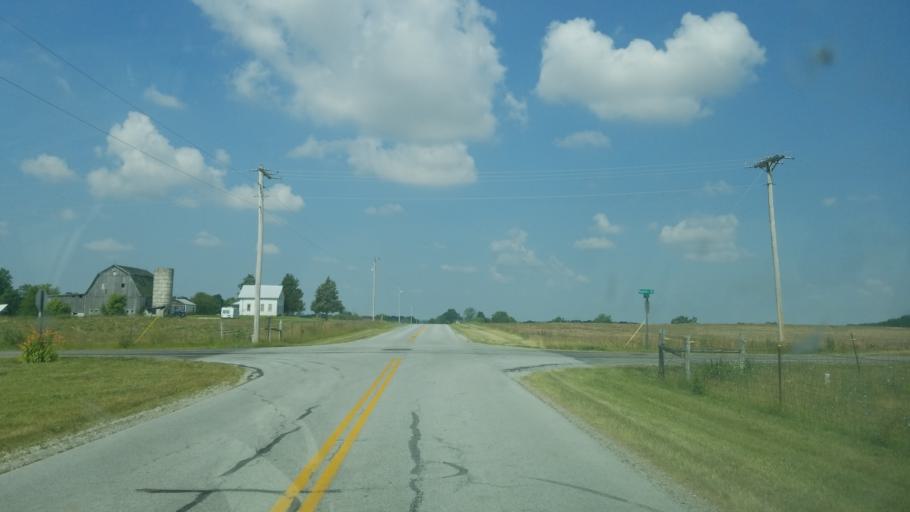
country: US
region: Ohio
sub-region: Shelby County
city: Jackson Center
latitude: 40.5714
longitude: -84.0453
